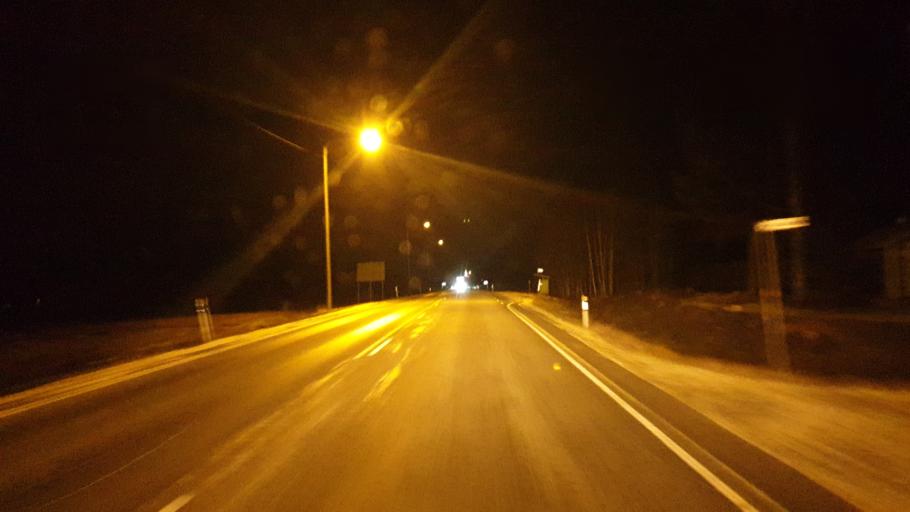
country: FI
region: Central Finland
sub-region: AEaenekoski
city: AEaenekoski
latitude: 62.7489
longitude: 25.7744
